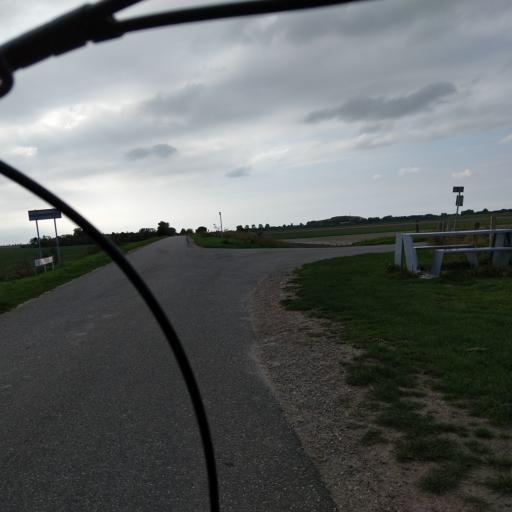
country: NL
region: South Holland
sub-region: Gemeente Goeree-Overflakkee
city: Ouddorp
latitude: 51.7295
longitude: 3.9443
